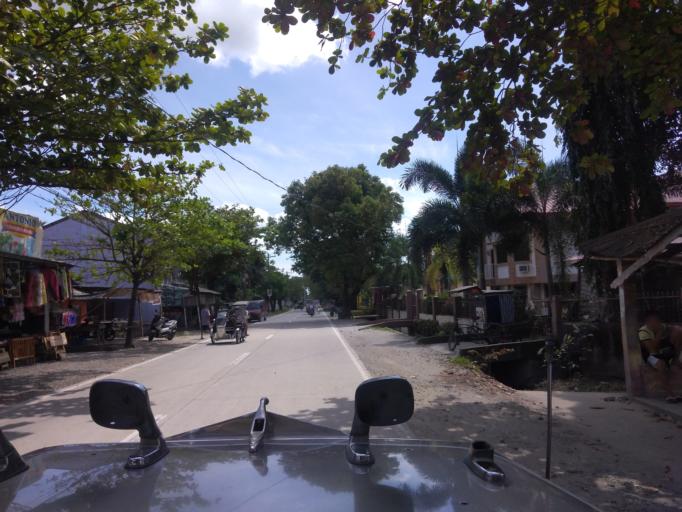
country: PH
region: Central Luzon
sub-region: Province of Pampanga
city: Santa Rita
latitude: 15.0100
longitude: 120.5938
